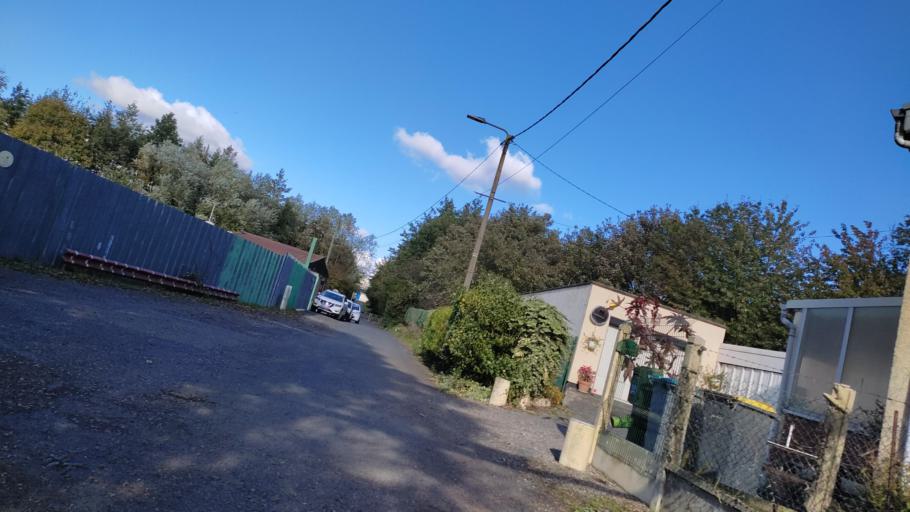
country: FR
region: Nord-Pas-de-Calais
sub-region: Departement du Pas-de-Calais
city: Saint-Laurent-Blangy
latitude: 50.3110
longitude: 2.8226
